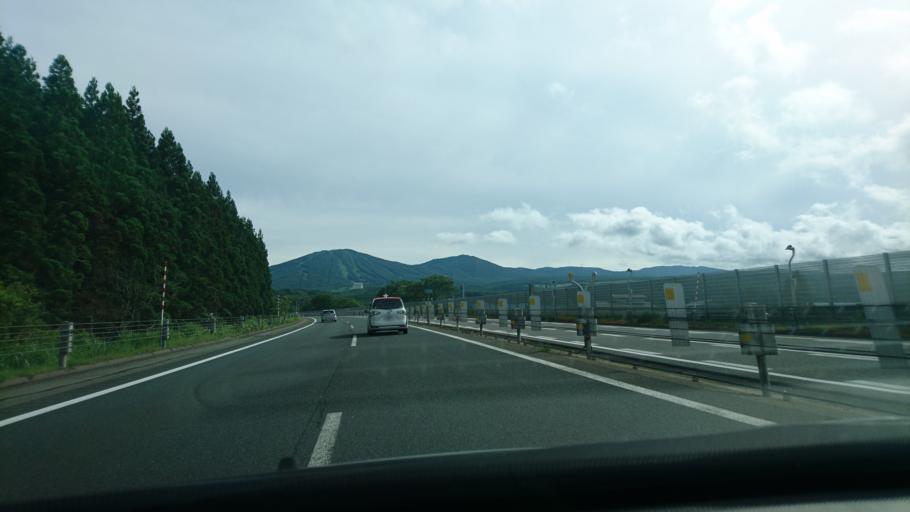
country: JP
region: Akita
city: Hanawa
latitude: 40.0304
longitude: 140.9840
